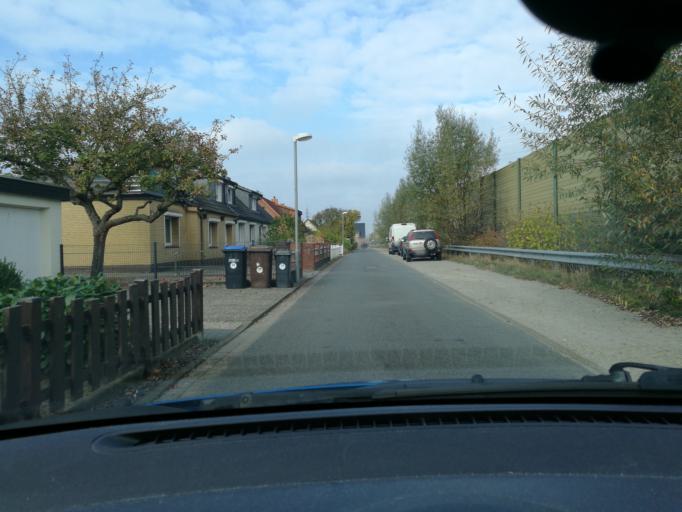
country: DE
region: Lower Saxony
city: Lueneburg
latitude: 53.2702
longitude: 10.4073
